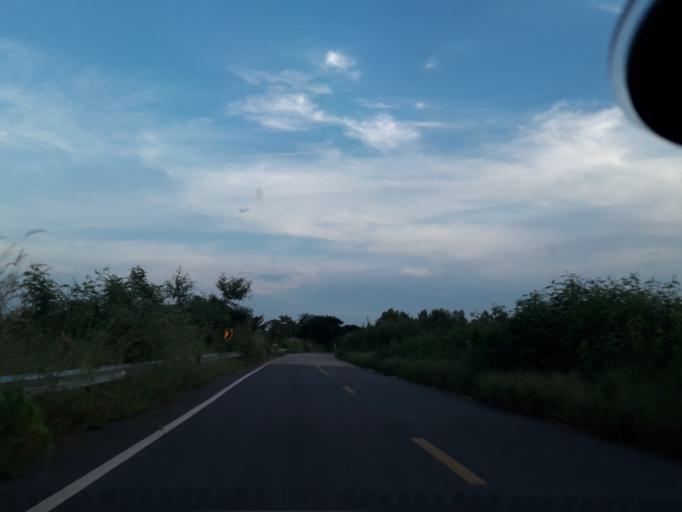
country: TH
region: Sara Buri
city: Nong Khae
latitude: 14.3010
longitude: 100.8899
